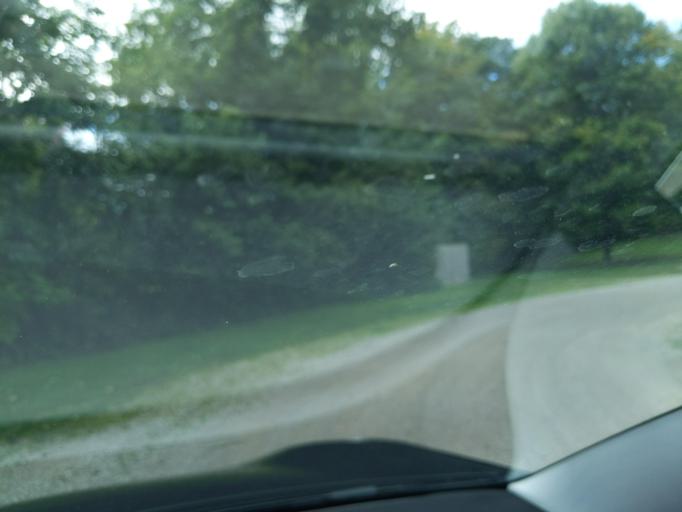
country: US
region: Michigan
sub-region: Antrim County
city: Bellaire
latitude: 45.0741
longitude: -85.3563
